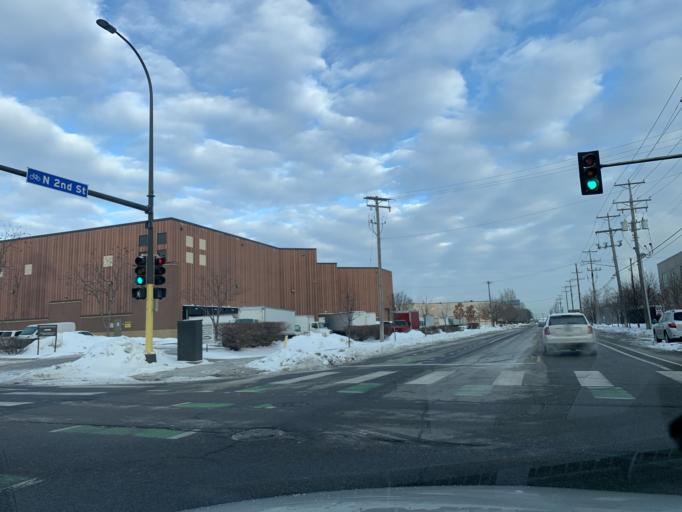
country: US
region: Minnesota
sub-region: Hennepin County
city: Minneapolis
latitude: 44.9920
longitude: -93.2798
